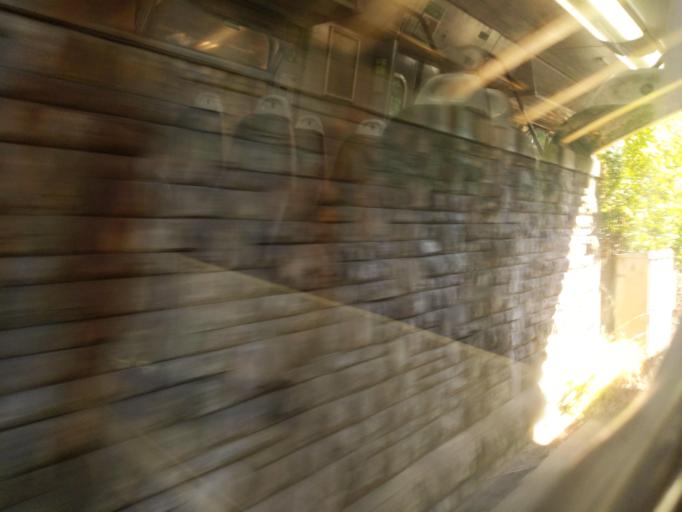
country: GB
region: England
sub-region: Borough of Torbay
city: Torquay
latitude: 50.4600
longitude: -3.5429
